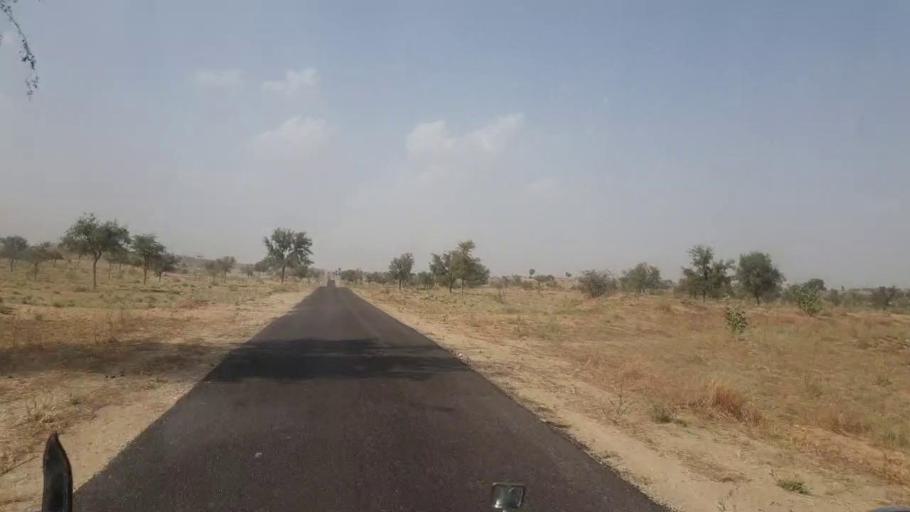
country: PK
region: Sindh
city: Islamkot
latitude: 25.1825
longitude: 70.2868
